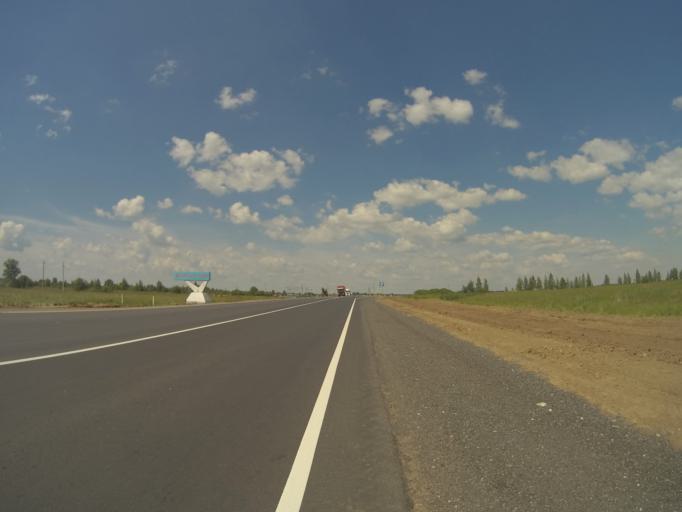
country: RU
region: Ivanovo
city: Privolzhsk
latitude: 57.3800
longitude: 41.2511
